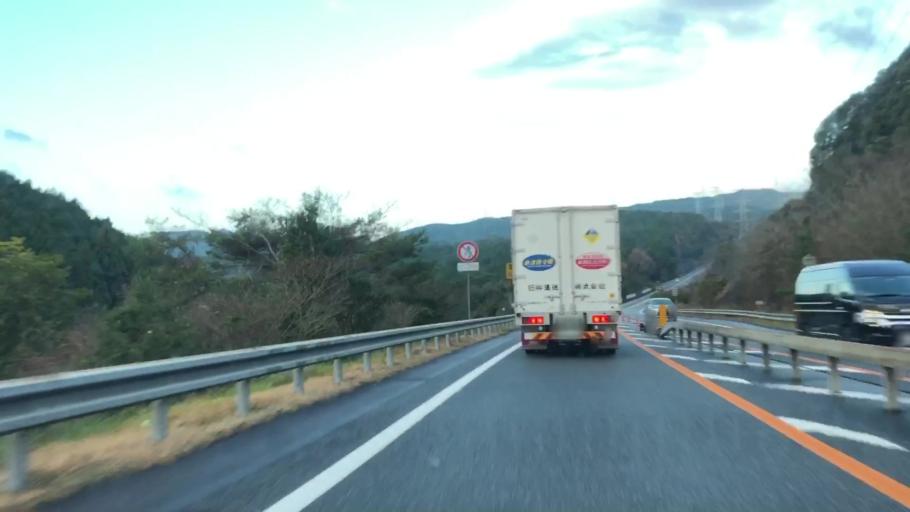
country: JP
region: Saga Prefecture
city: Imaricho-ko
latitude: 33.1546
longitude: 129.8821
